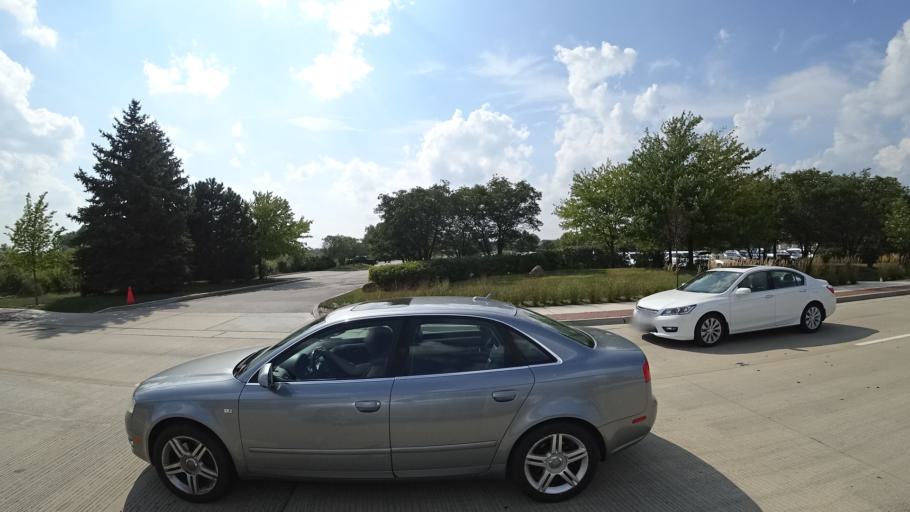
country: US
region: Illinois
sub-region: Cook County
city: Orland Park
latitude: 41.6091
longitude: -87.8532
